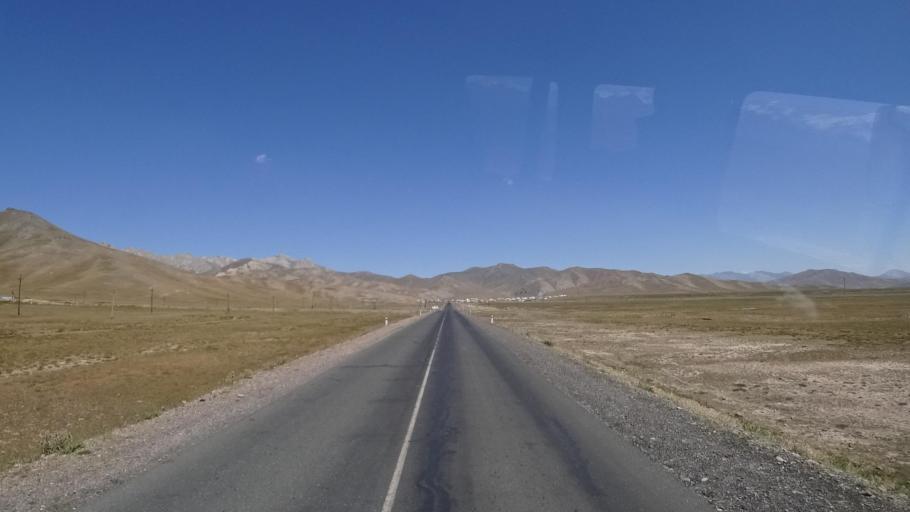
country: KG
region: Osh
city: Gul'cha
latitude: 39.7106
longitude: 73.2346
